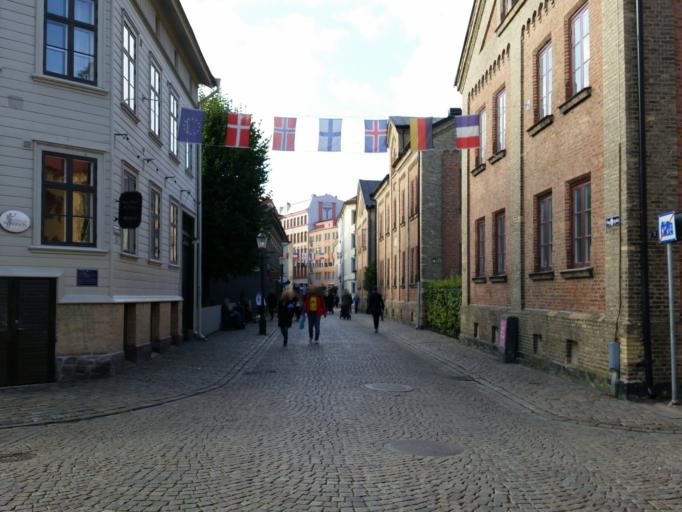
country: SE
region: Vaestra Goetaland
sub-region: Goteborg
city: Goeteborg
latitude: 57.6986
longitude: 11.9554
